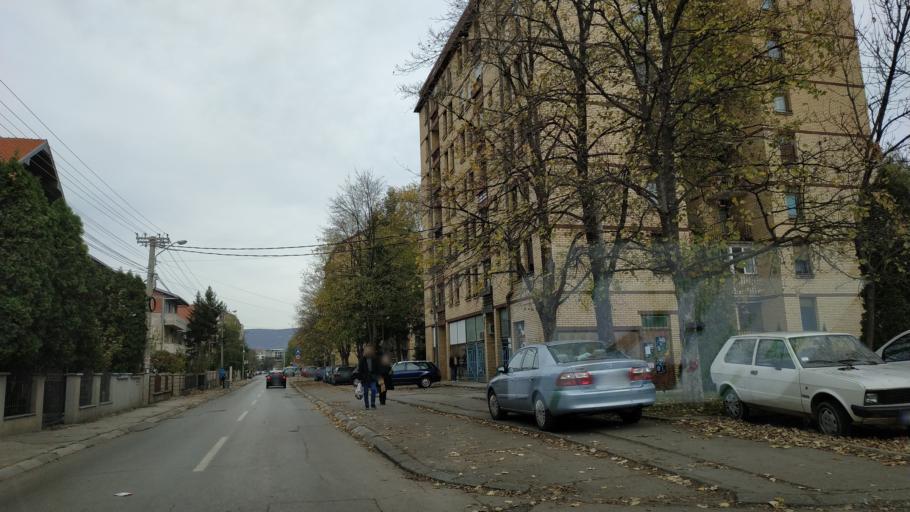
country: RS
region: Central Serbia
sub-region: Nisavski Okrug
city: Nis
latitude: 43.3169
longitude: 21.9349
